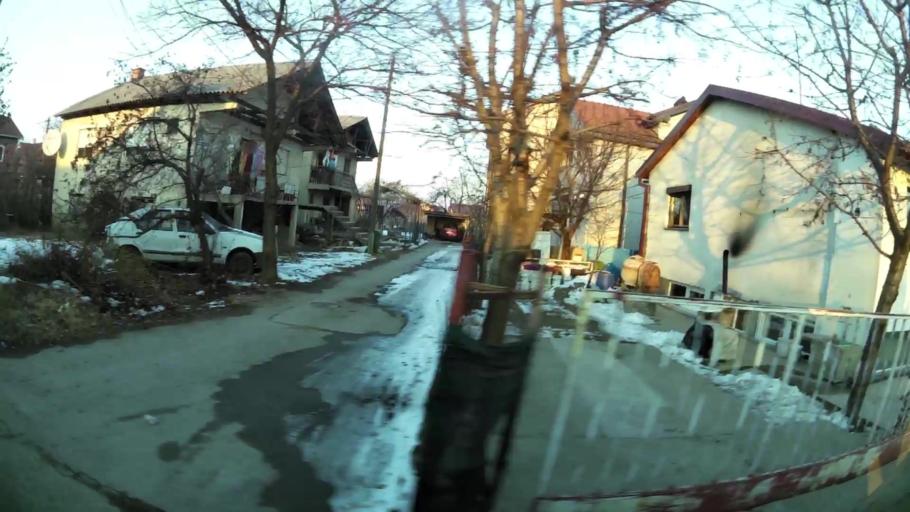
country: MK
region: Kisela Voda
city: Kisela Voda
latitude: 41.9796
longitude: 21.4909
